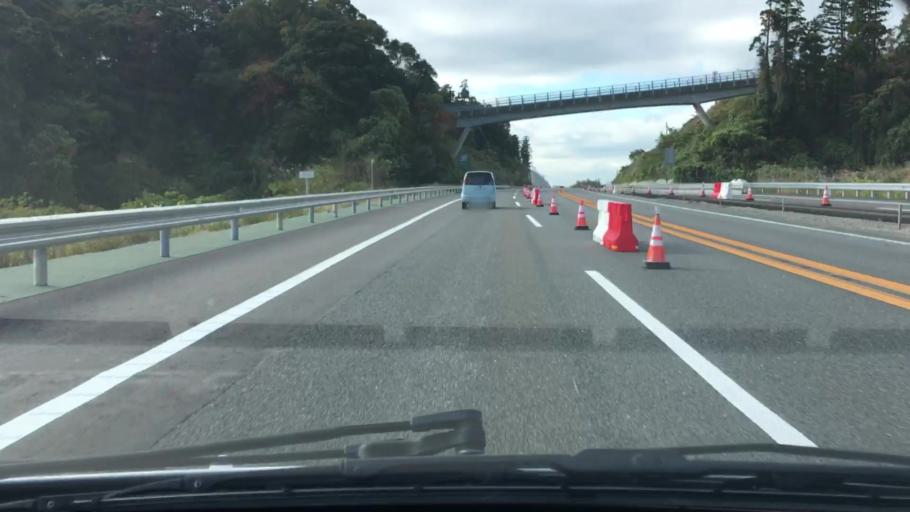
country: JP
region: Chiba
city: Kimitsu
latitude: 35.2730
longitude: 139.9179
